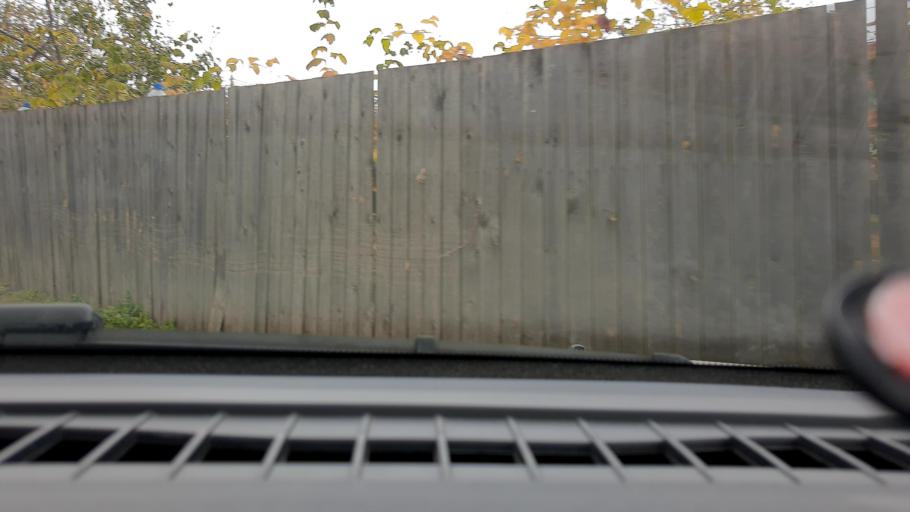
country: RU
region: Nizjnij Novgorod
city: Nizhniy Novgorod
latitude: 56.2698
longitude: 43.9575
